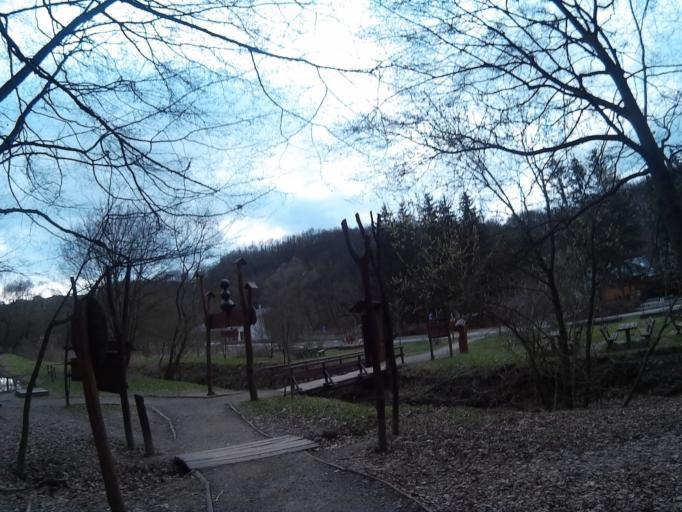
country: HU
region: Pest
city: Veroce
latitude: 47.8499
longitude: 19.1059
